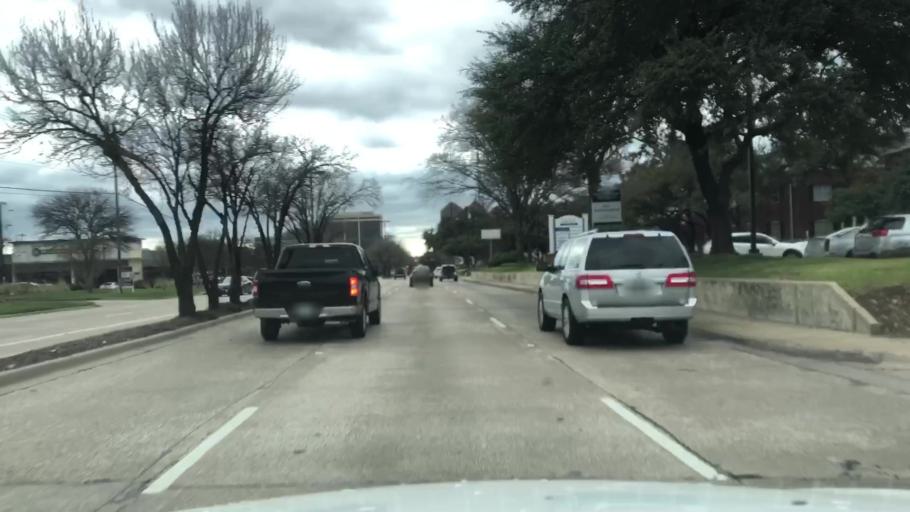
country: US
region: Texas
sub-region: Dallas County
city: Addison
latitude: 32.9489
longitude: -96.8391
